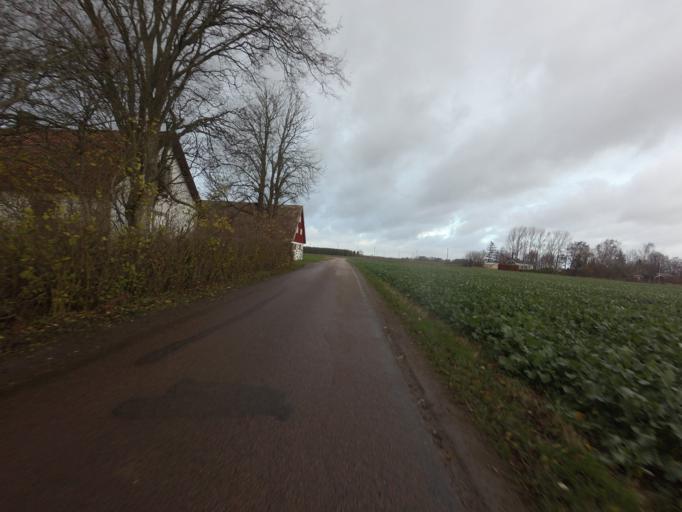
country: SE
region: Skane
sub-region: Helsingborg
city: Odakra
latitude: 56.1384
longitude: 12.7647
